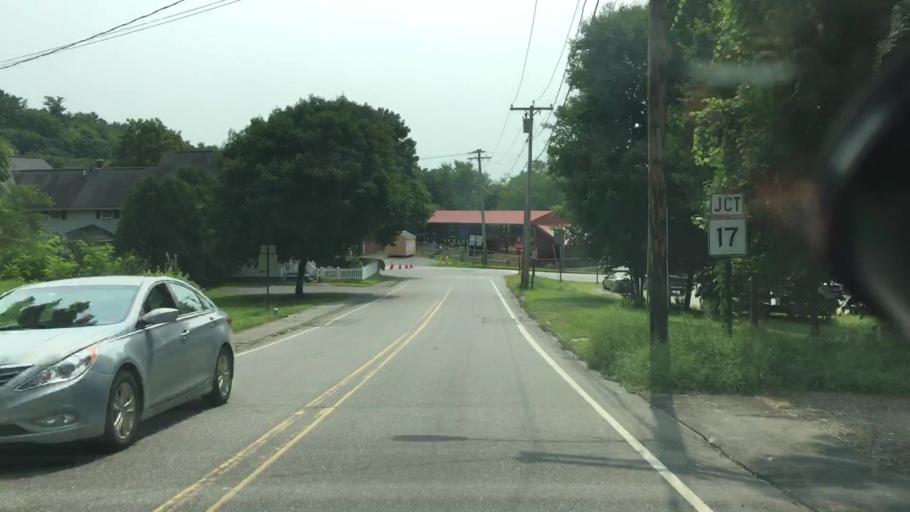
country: US
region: Maine
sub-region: Androscoggin County
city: Livermore Falls
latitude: 44.4737
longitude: -70.1866
